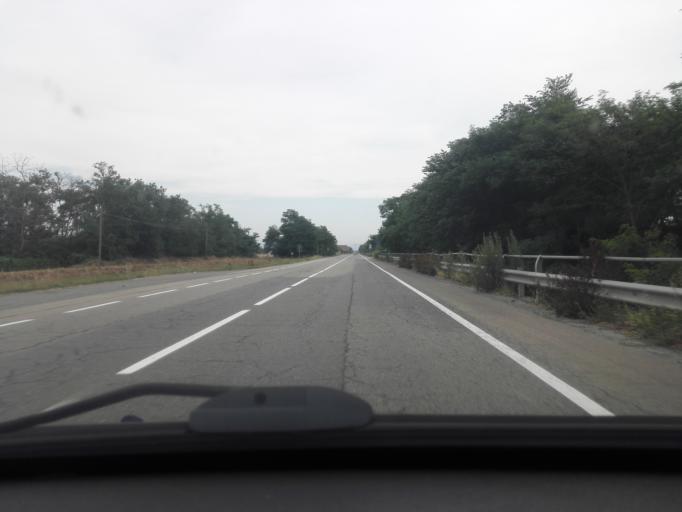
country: IT
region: Piedmont
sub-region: Provincia di Alessandria
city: Litta Parodi-Cascinagrossa
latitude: 44.8476
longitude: 8.7227
